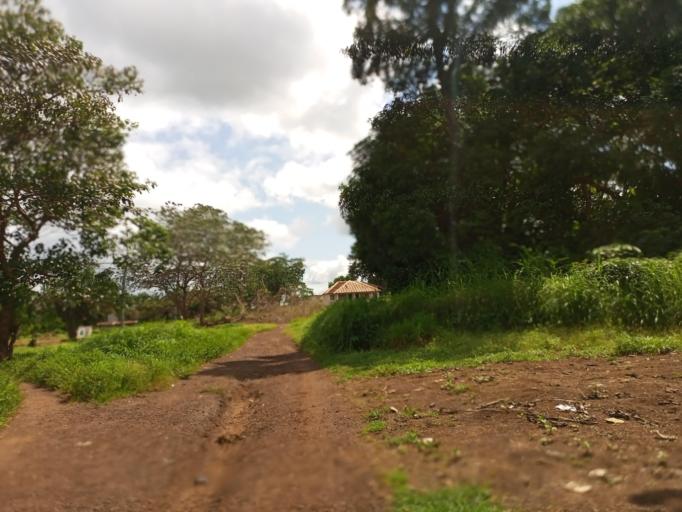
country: SL
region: Northern Province
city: Kamakwie
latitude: 9.4964
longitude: -12.2362
